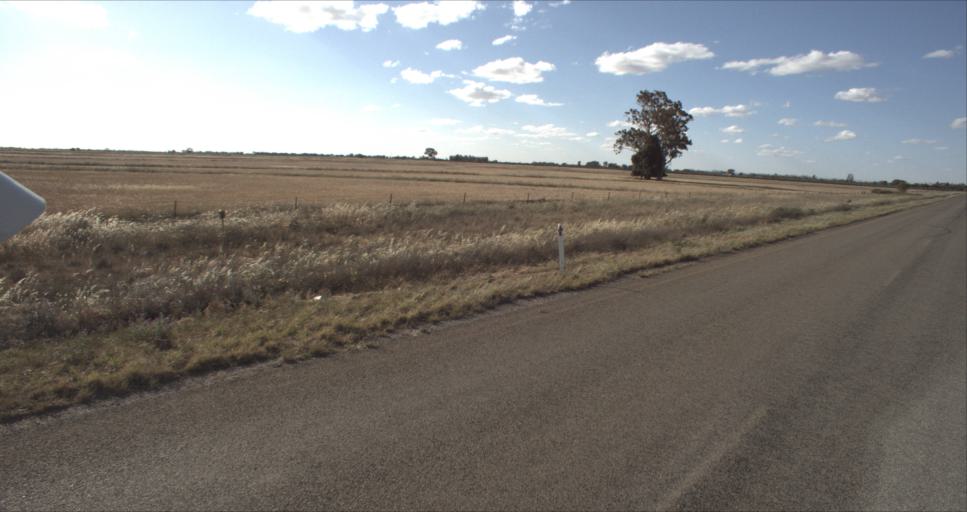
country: AU
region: New South Wales
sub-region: Leeton
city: Leeton
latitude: -34.5372
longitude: 146.2803
